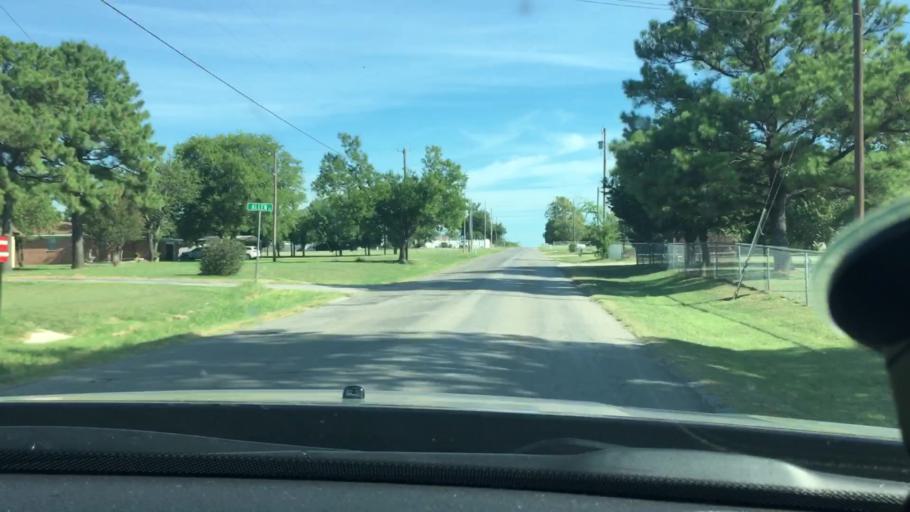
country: US
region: Oklahoma
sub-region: Carter County
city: Lone Grove
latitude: 34.1832
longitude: -97.2475
